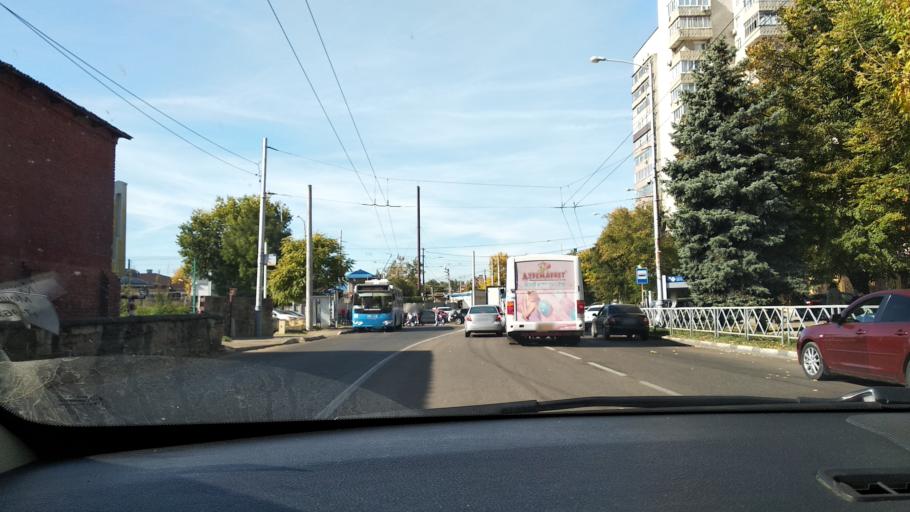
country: RU
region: Adygeya
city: Yablonovskiy
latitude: 45.0133
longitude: 38.9612
